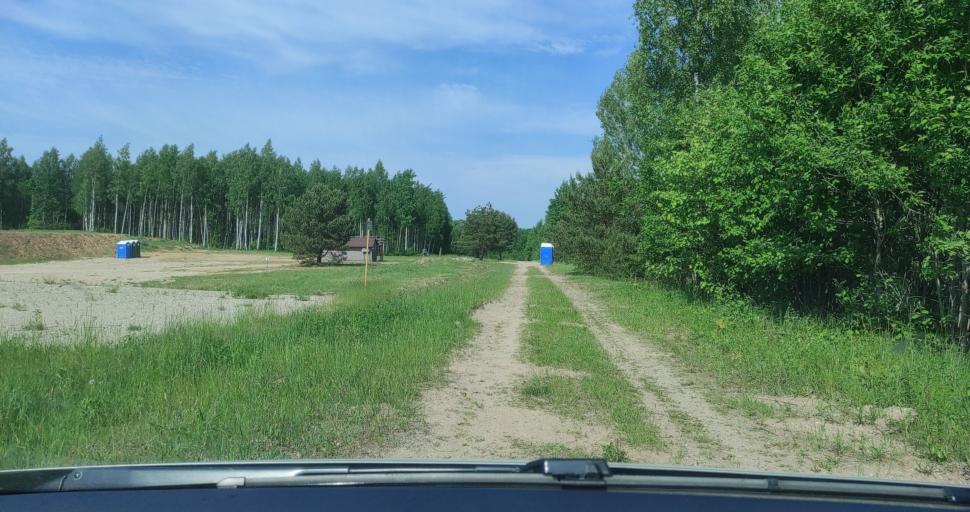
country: LV
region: Kuldigas Rajons
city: Kuldiga
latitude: 56.9376
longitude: 21.9191
